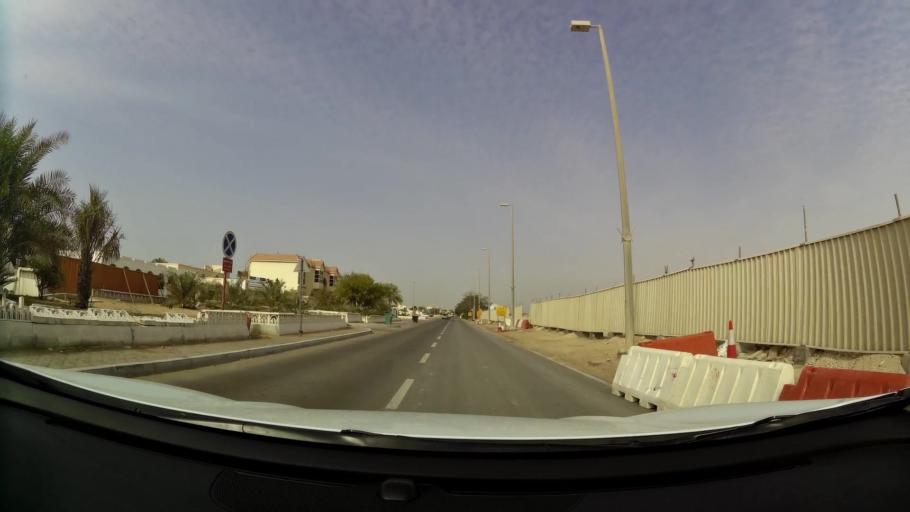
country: AE
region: Abu Dhabi
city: Abu Dhabi
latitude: 24.5934
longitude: 54.7009
